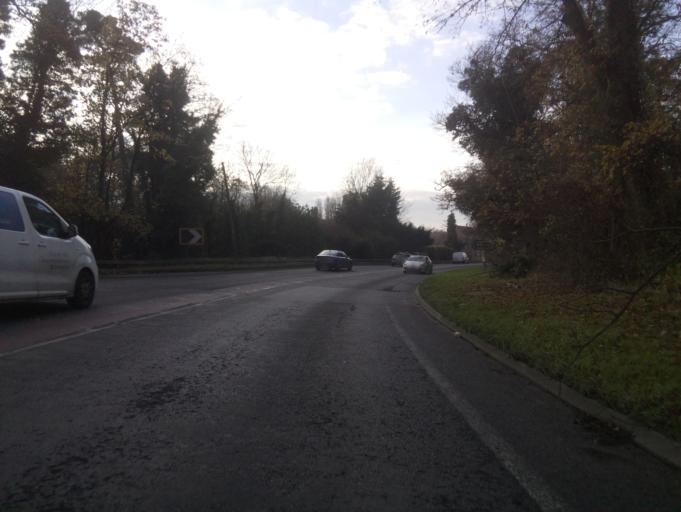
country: GB
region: England
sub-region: Warwickshire
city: Curdworth
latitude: 52.5605
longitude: -1.7413
